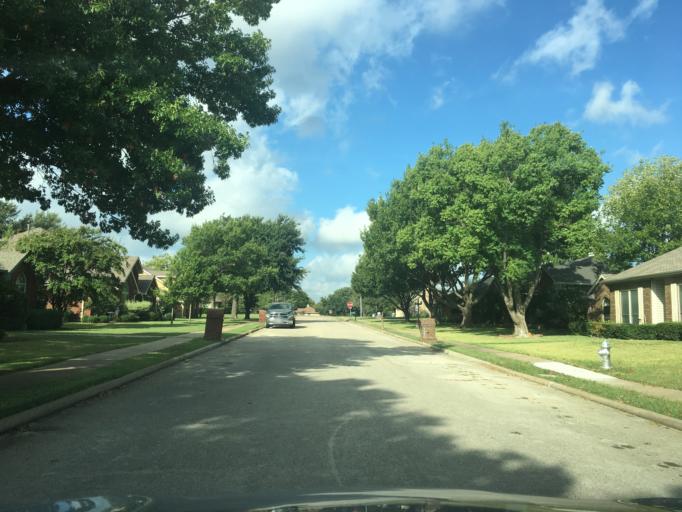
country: US
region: Texas
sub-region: Dallas County
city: Sachse
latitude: 32.9697
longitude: -96.5896
